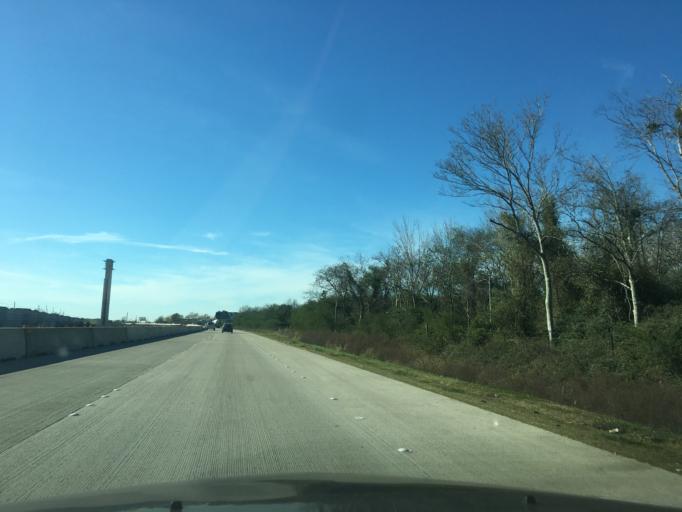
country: US
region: Texas
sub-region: Fort Bend County
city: Rosenberg
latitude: 29.5352
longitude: -95.8476
